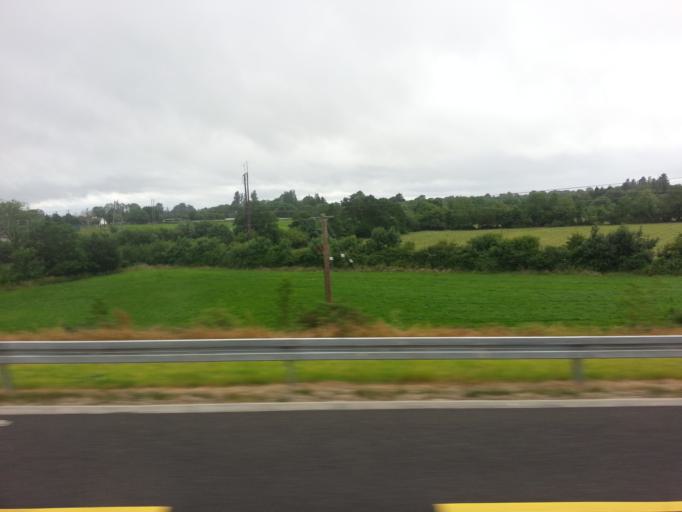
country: IE
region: Leinster
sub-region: Kilkenny
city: Kilkenny
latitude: 52.6425
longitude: -7.1724
